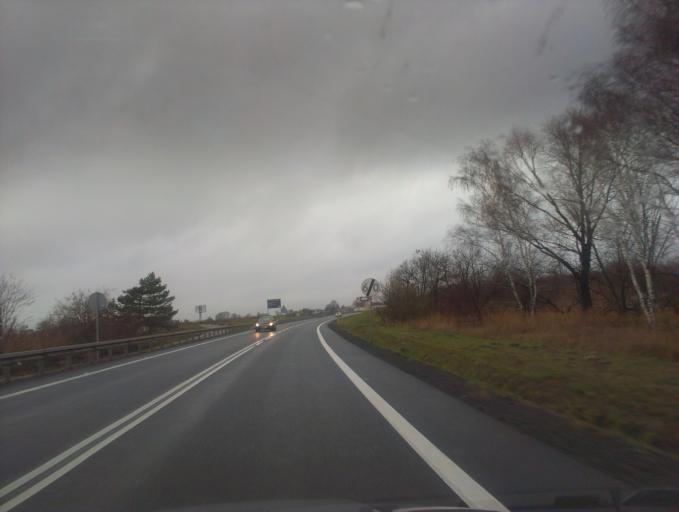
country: PL
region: Greater Poland Voivodeship
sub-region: Powiat poznanski
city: Zlotniki
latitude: 52.5536
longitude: 16.8357
